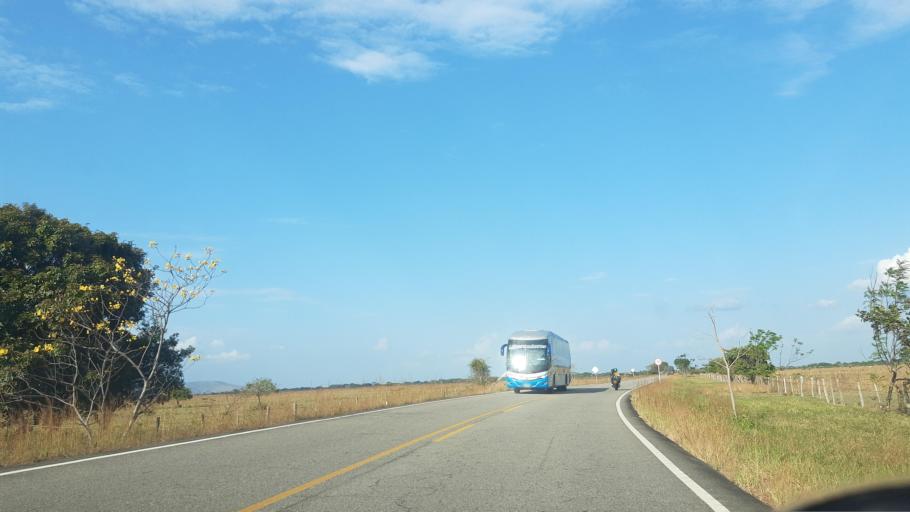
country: CO
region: Casanare
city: Municipio Hato Corozal
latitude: 6.1382
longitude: -71.7810
